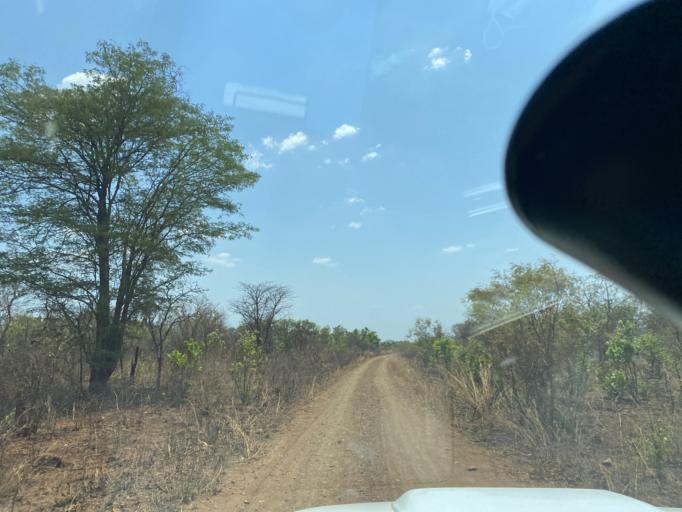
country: ZM
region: Lusaka
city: Lusaka
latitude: -15.5086
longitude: 27.9894
